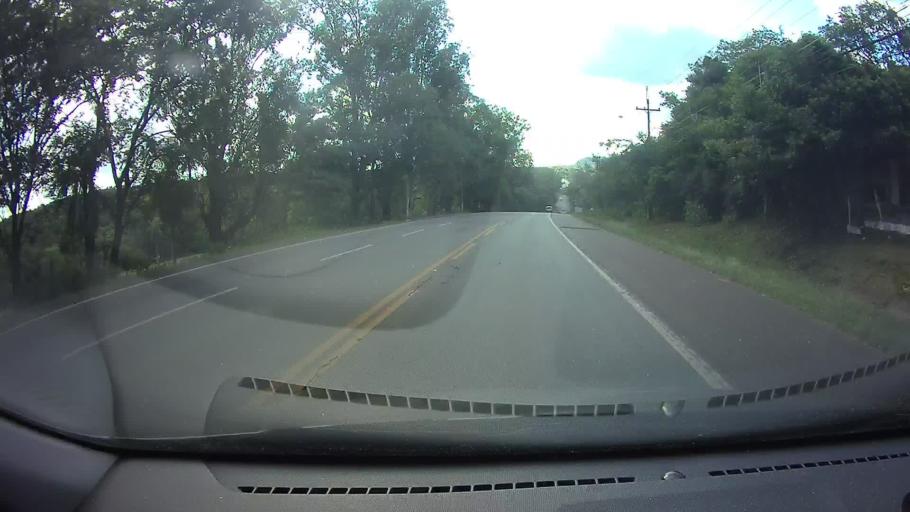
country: PY
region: Cordillera
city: Caacupe
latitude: -25.3870
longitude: -57.1185
